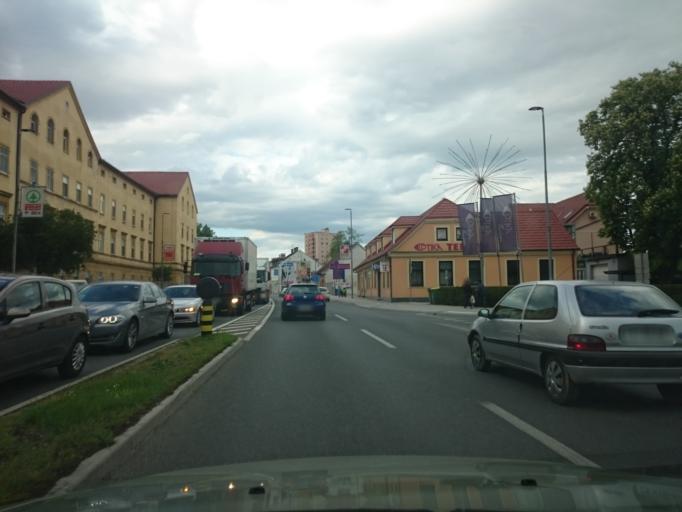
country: SI
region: Celje
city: Celje
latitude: 46.2358
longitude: 15.2714
